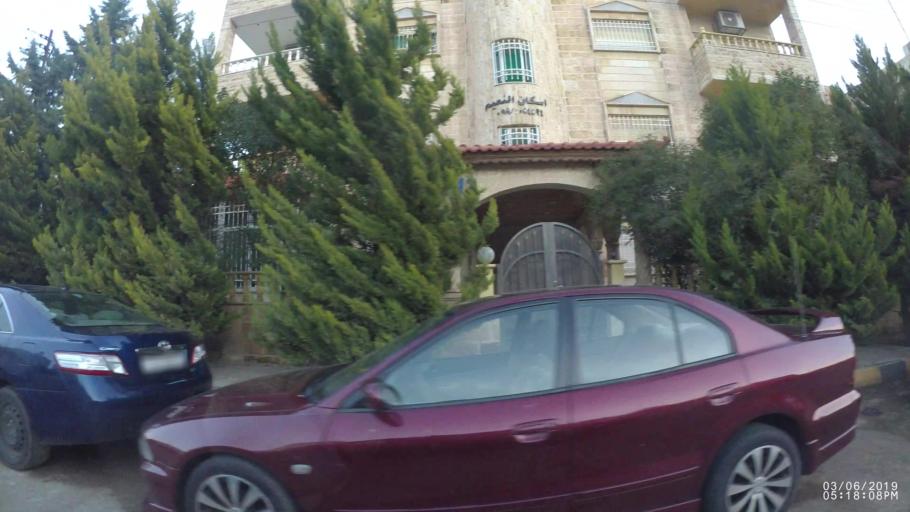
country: JO
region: Amman
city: Amman
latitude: 31.9975
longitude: 35.9506
